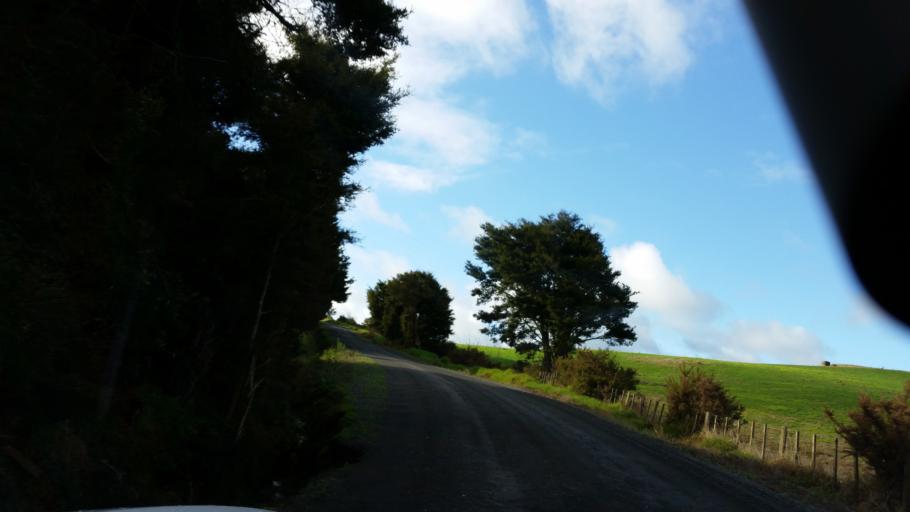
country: NZ
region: Northland
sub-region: Whangarei
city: Maungatapere
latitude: -35.6930
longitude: 174.1115
